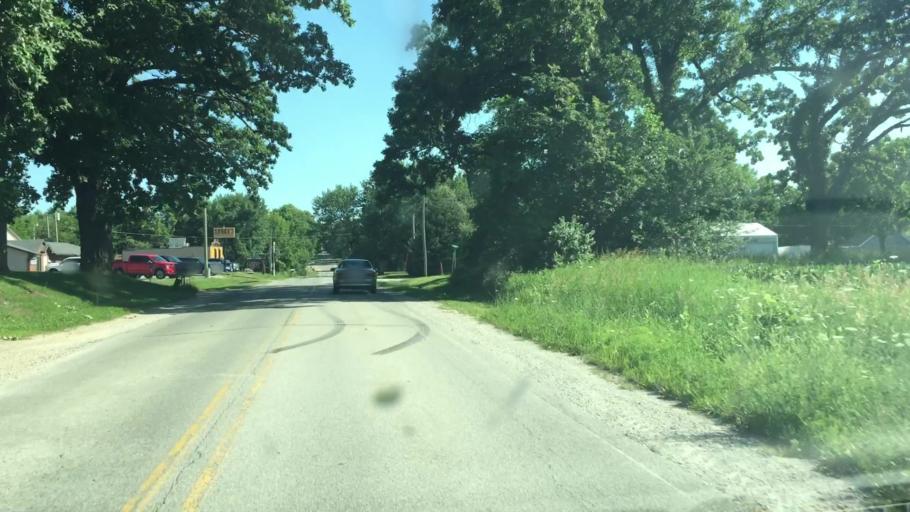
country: US
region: Iowa
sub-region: Linn County
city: Ely
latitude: 41.8517
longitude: -91.6462
